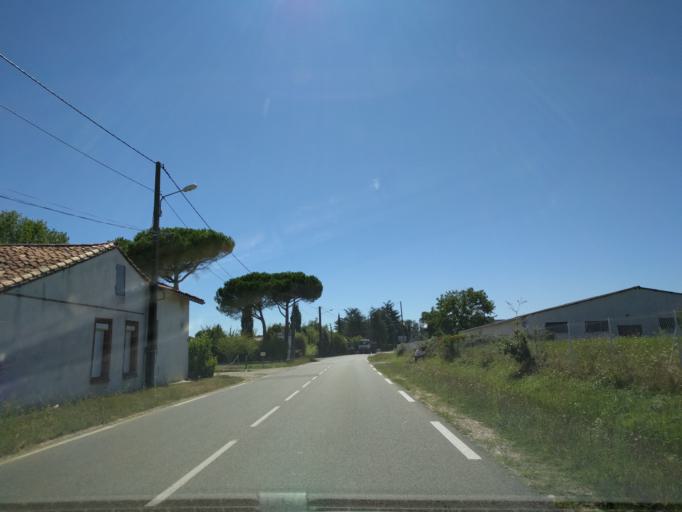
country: FR
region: Midi-Pyrenees
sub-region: Departement du Tarn-et-Garonne
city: Montauban
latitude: 44.0268
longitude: 1.3803
